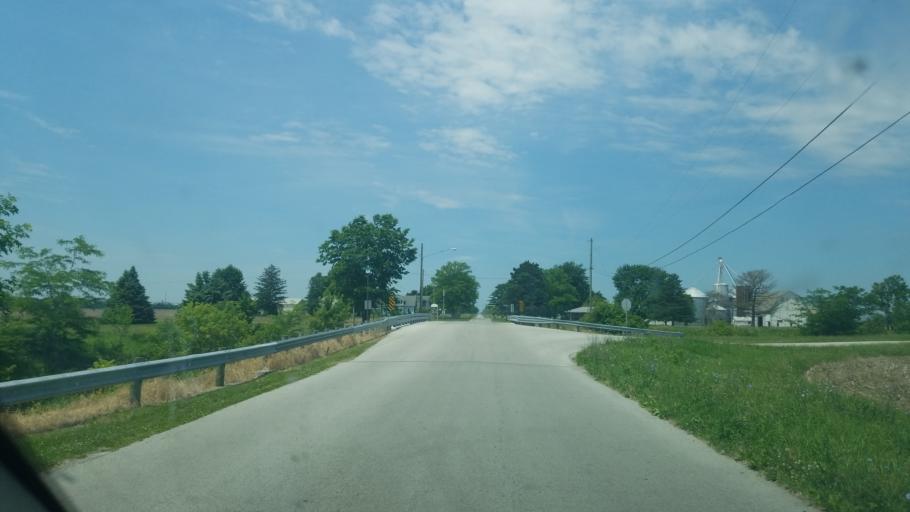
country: US
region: Ohio
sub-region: Wood County
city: North Baltimore
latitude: 41.2538
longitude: -83.6104
